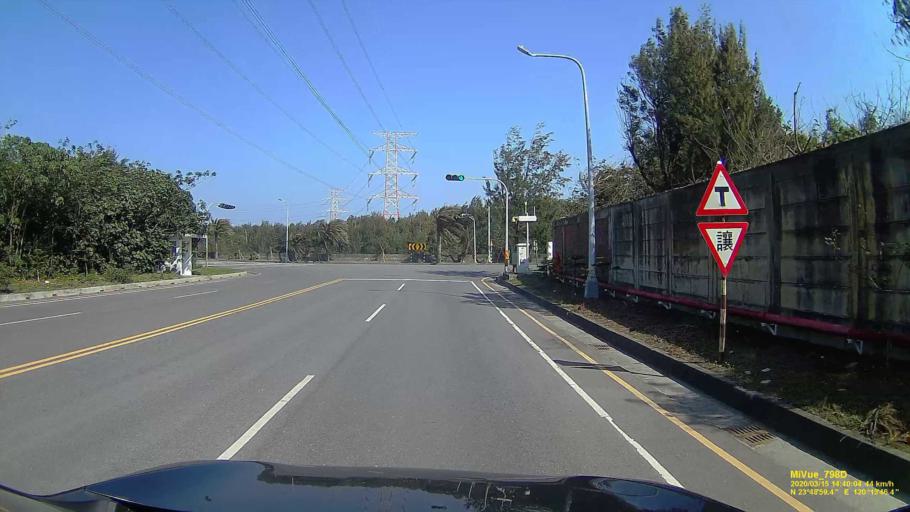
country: TW
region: Taiwan
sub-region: Yunlin
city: Douliu
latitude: 23.8164
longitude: 120.2297
